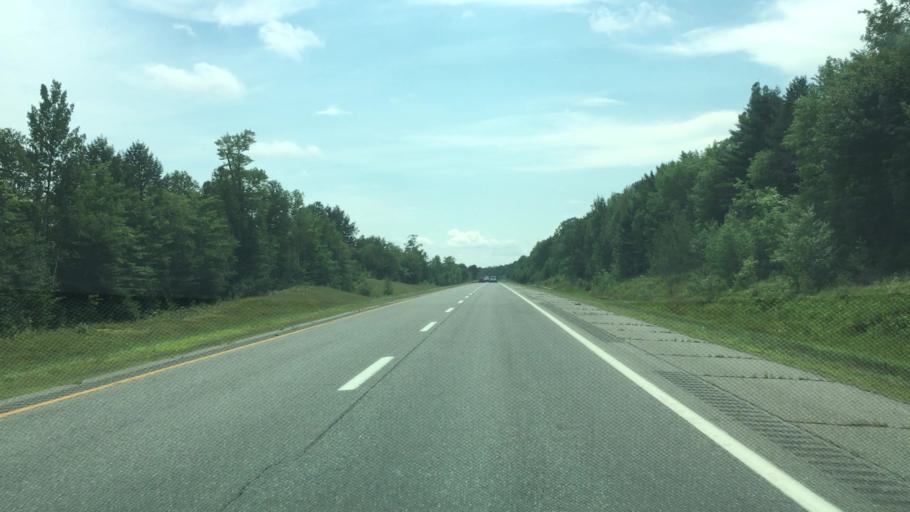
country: US
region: Maine
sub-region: Penobscot County
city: Medway
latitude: 45.5606
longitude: -68.5482
